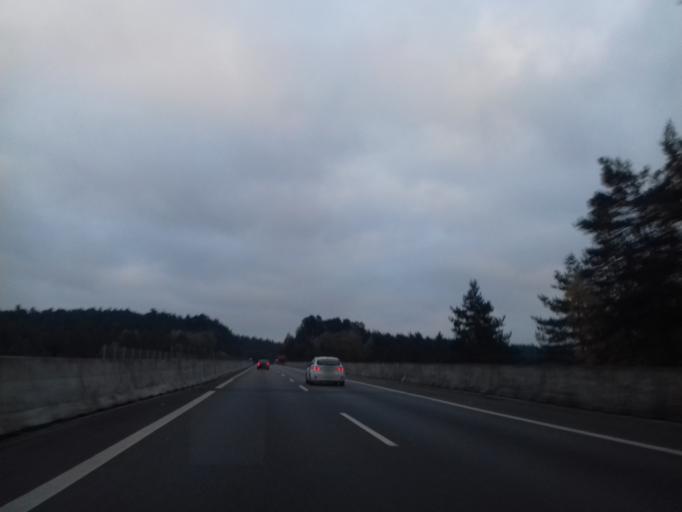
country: CZ
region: Central Bohemia
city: Zruc nad Sazavou
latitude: 49.6890
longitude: 15.0992
